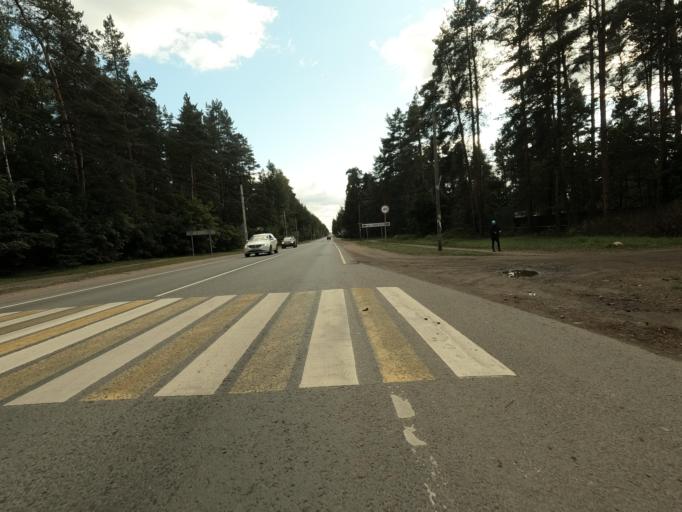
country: RU
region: Leningrad
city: Vsevolozhsk
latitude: 60.0073
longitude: 30.6646
